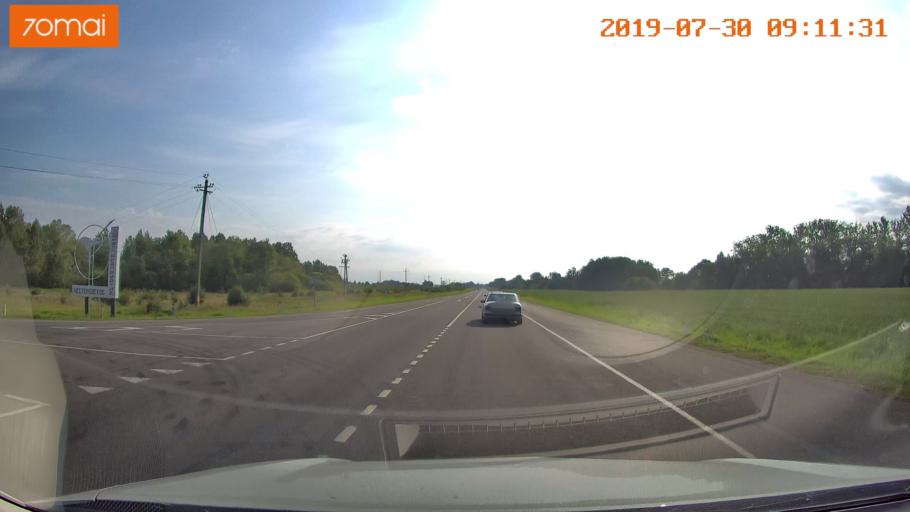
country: RU
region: Kaliningrad
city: Nesterov
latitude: 54.6130
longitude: 22.4515
